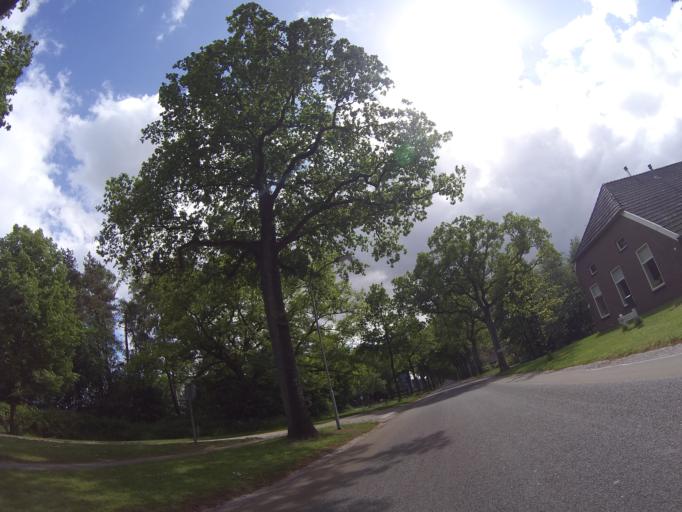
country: NL
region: Drenthe
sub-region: Gemeente Borger-Odoorn
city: Borger
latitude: 52.8770
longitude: 6.8665
